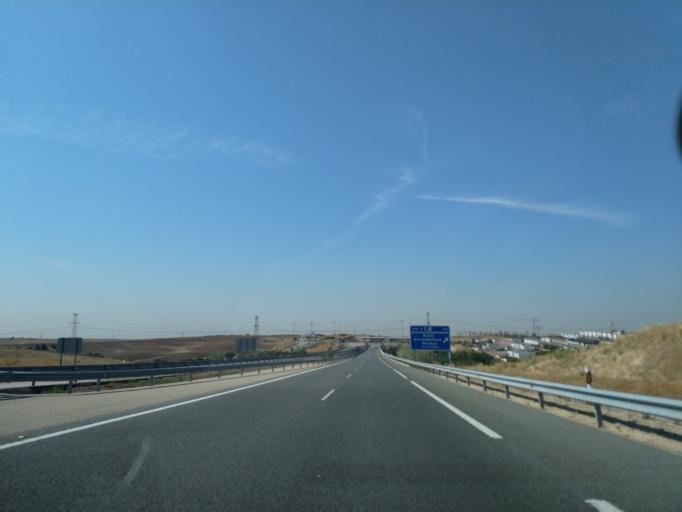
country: ES
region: Madrid
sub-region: Provincia de Madrid
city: Arroyomolinos
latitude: 40.2634
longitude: -3.9027
